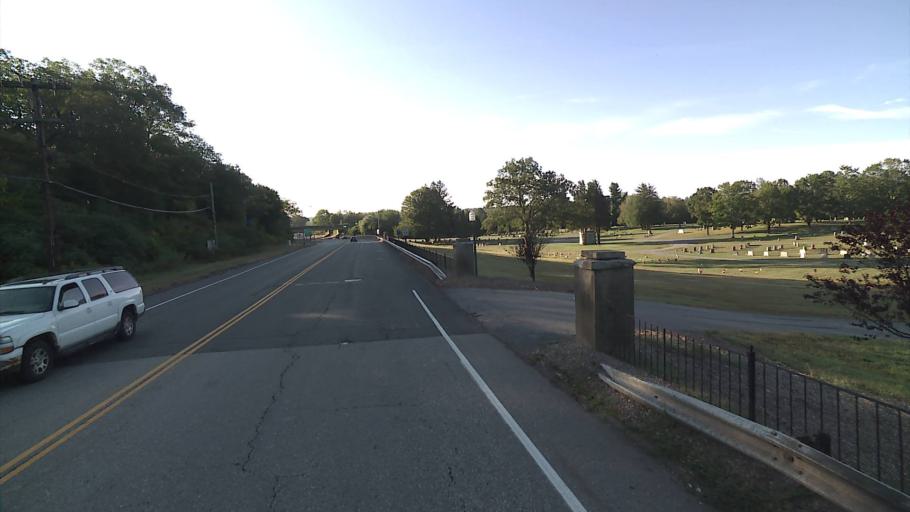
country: US
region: Connecticut
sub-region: Tolland County
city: Mansfield City
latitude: 41.7282
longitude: -72.2451
